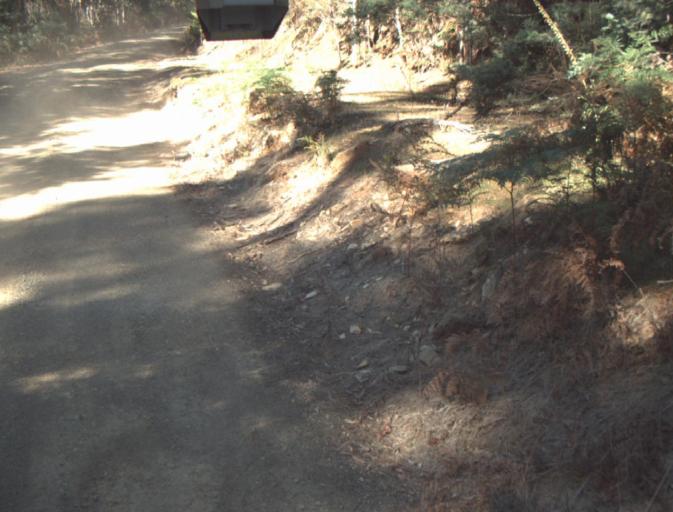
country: AU
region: Tasmania
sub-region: Dorset
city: Scottsdale
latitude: -41.2801
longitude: 147.3585
